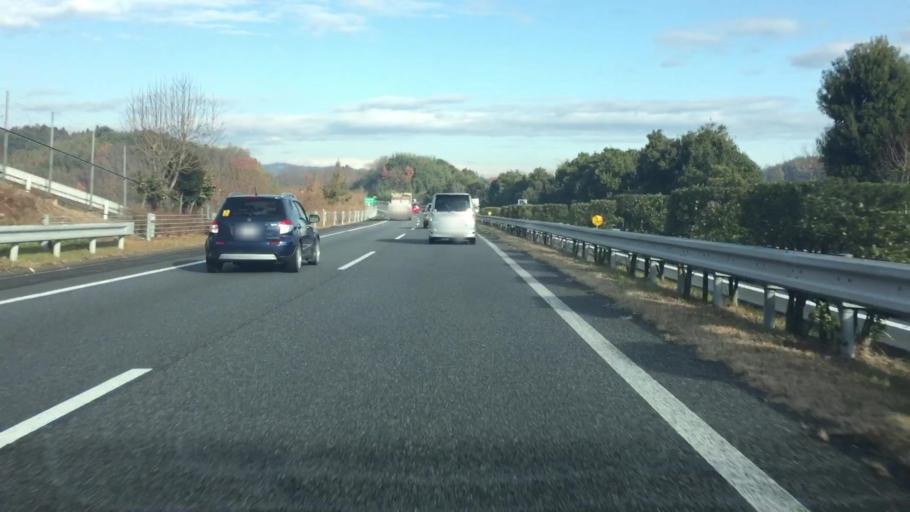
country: JP
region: Gunma
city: Tomioka
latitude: 36.2727
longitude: 138.8126
